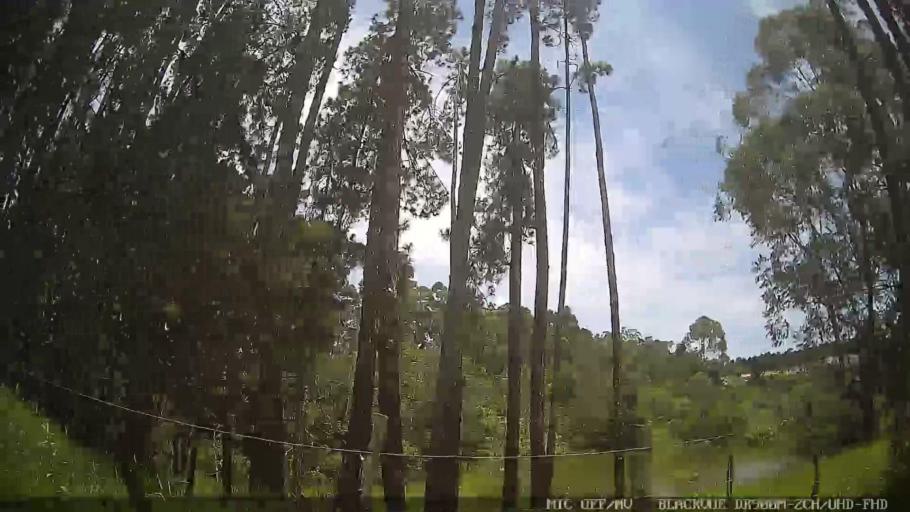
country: BR
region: Sao Paulo
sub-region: Atibaia
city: Atibaia
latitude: -23.0834
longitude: -46.6181
